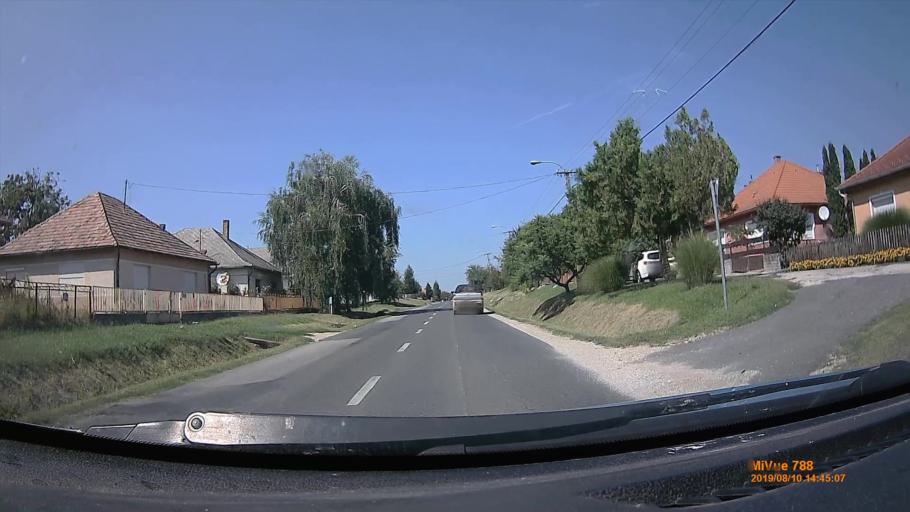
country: HU
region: Somogy
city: Somogyvar
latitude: 46.5823
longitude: 17.6458
